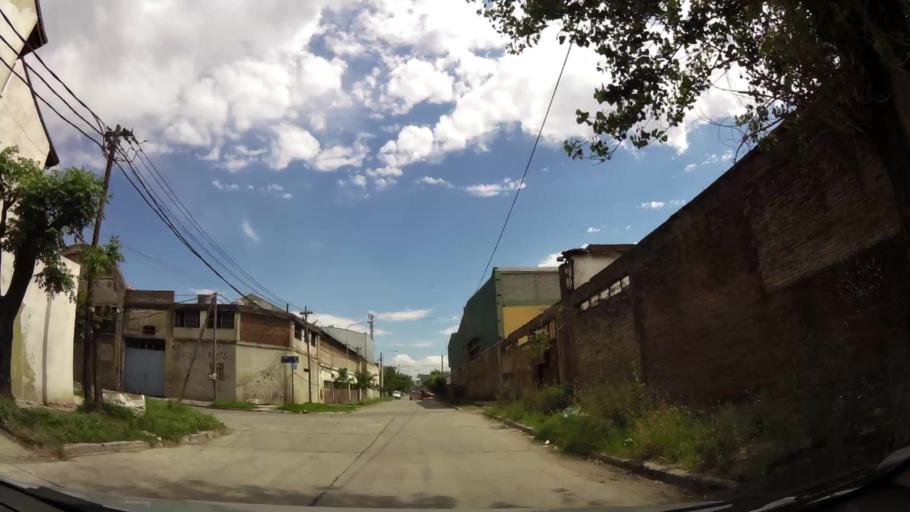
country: AR
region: Buenos Aires
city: San Justo
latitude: -34.6801
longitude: -58.5468
